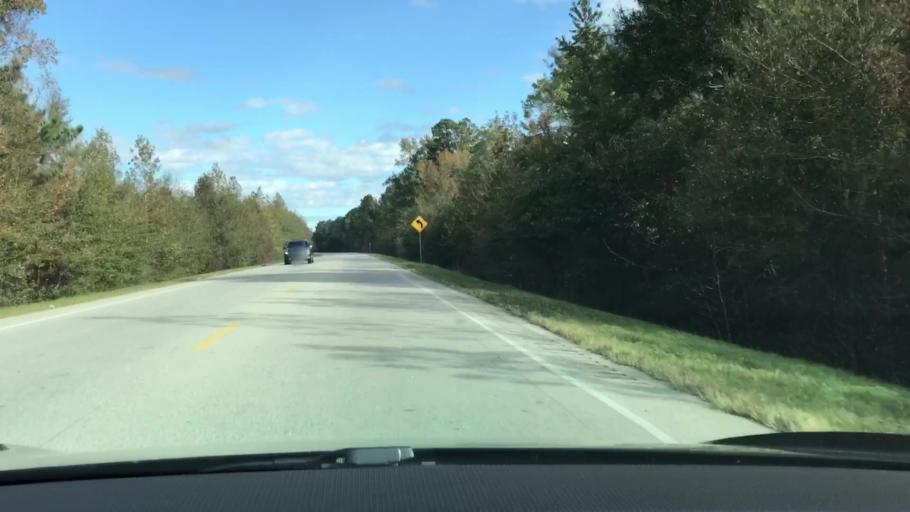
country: US
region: Georgia
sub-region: Jefferson County
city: Louisville
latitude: 32.9555
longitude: -82.3929
